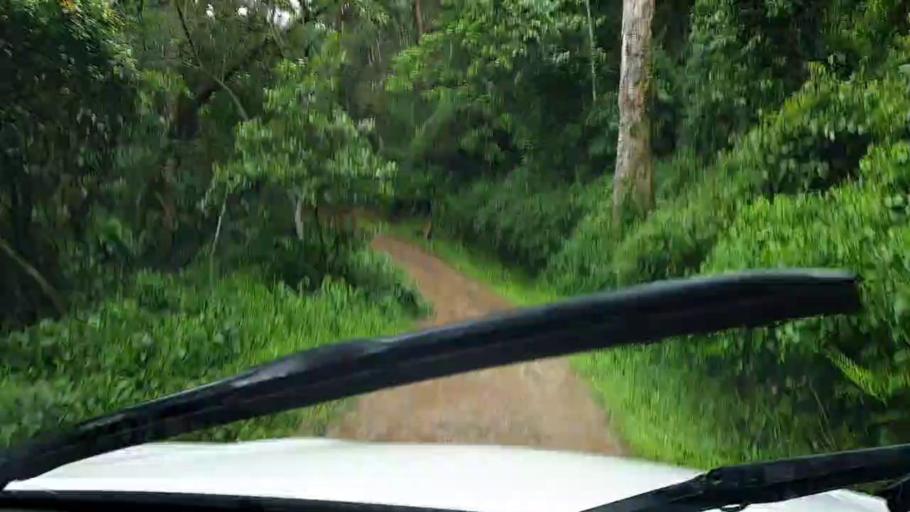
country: RW
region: Western Province
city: Cyangugu
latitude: -2.5586
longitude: 28.9886
